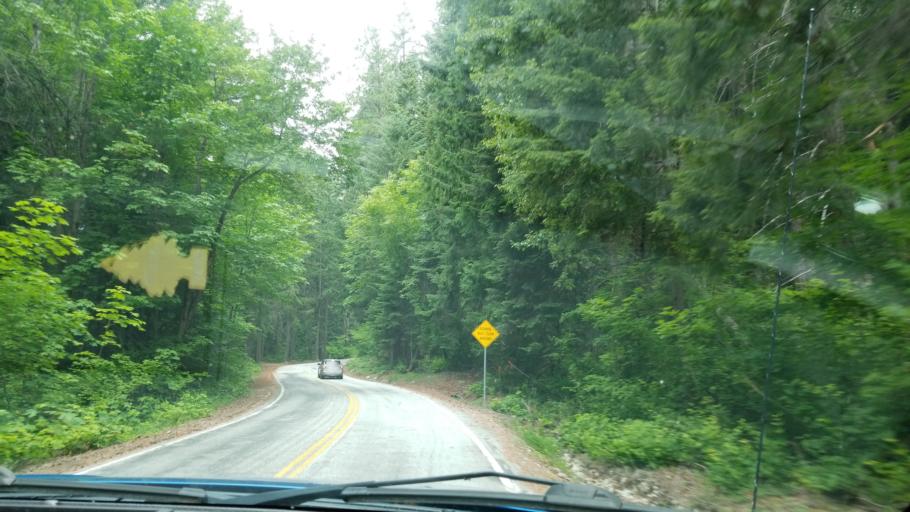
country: US
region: Washington
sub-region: Chelan County
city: Leavenworth
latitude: 47.8523
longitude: -120.8348
